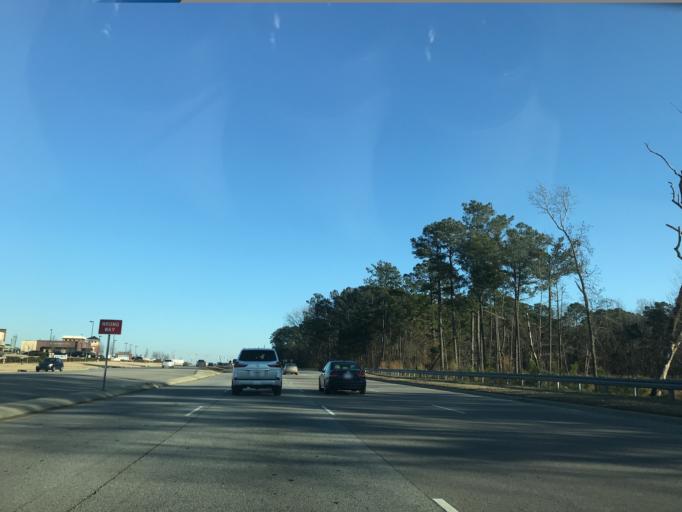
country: US
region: North Carolina
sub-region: Wake County
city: Garner
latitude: 35.6975
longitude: -78.5892
